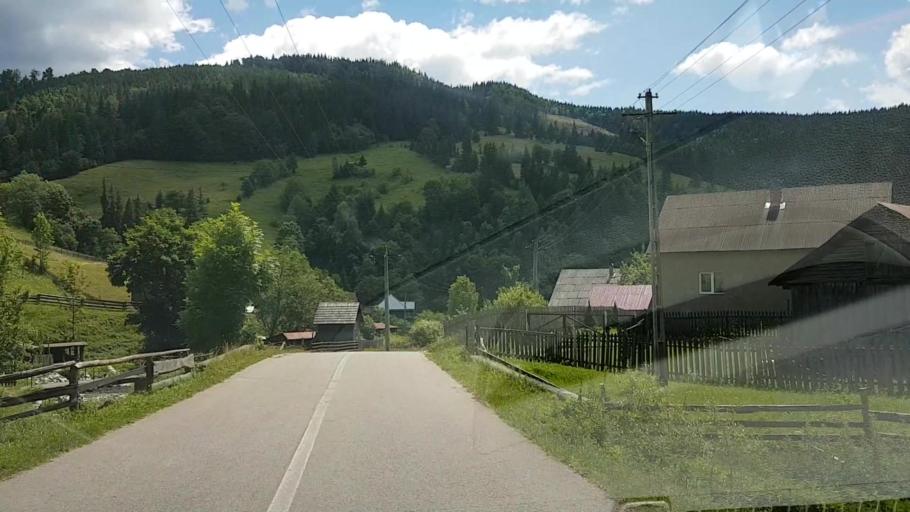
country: RO
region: Suceava
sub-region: Comuna Crucea
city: Crucea
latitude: 47.4174
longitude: 25.5831
